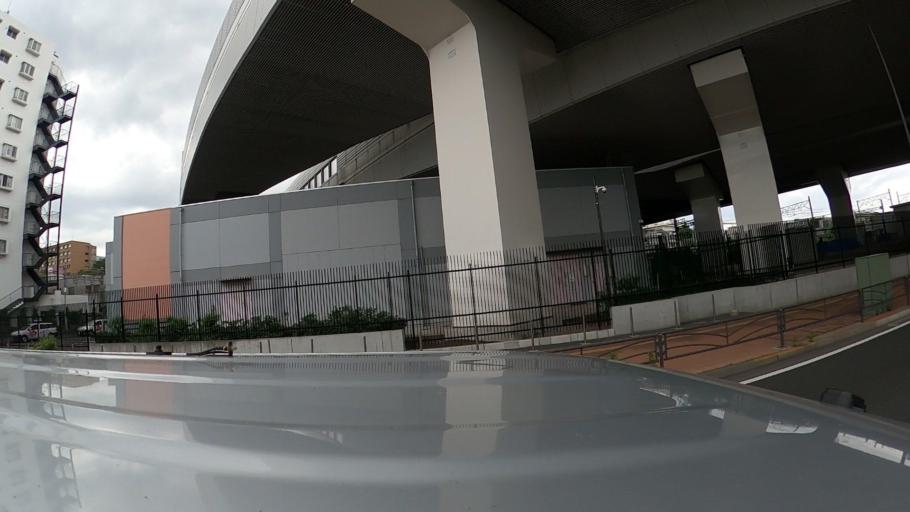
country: JP
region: Kanagawa
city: Yokohama
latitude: 35.4912
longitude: 139.6619
